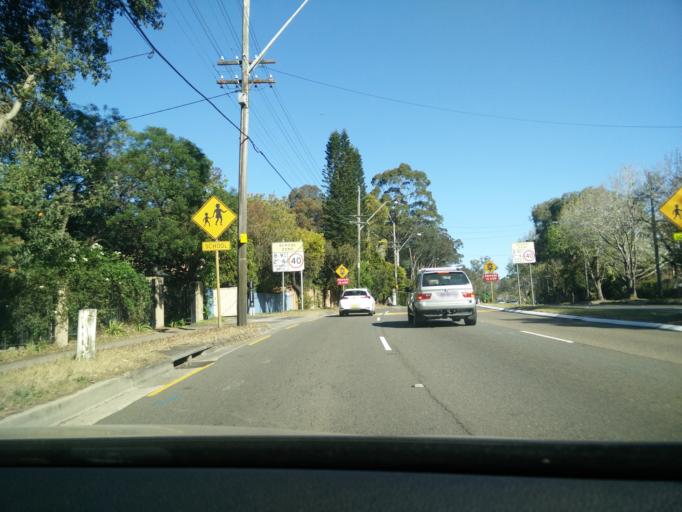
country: AU
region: New South Wales
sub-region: City of Sydney
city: Pymble
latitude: -33.7587
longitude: 151.1382
